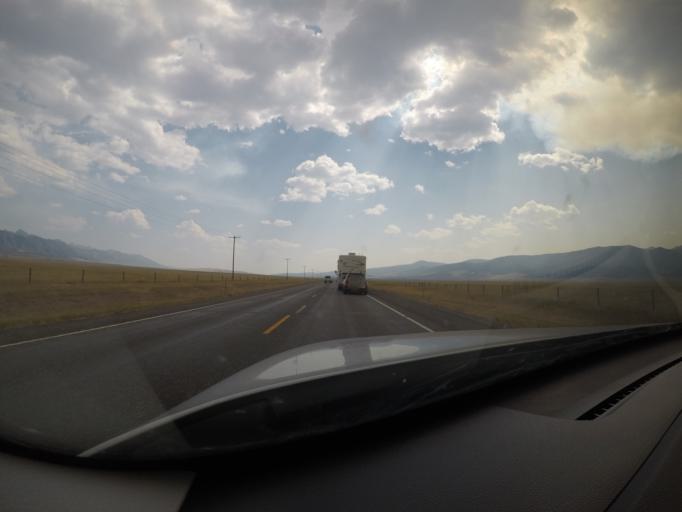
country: US
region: Montana
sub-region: Gallatin County
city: Big Sky
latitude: 45.0348
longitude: -111.6482
